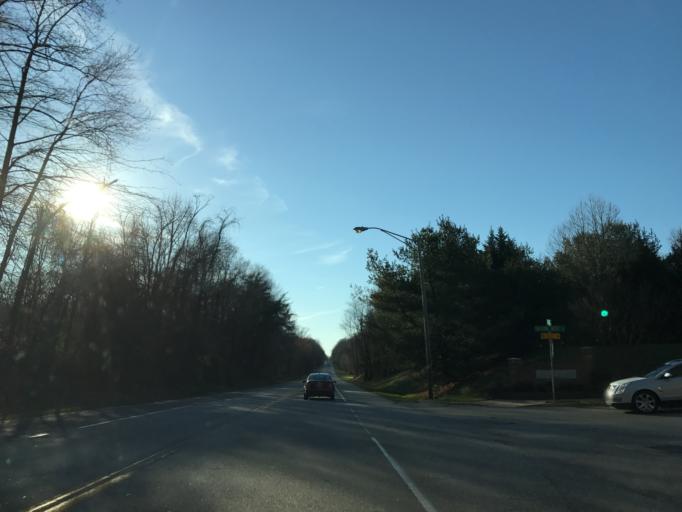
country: US
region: Maryland
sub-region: Anne Arundel County
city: Cape Saint Claire
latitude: 39.0362
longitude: -76.4677
